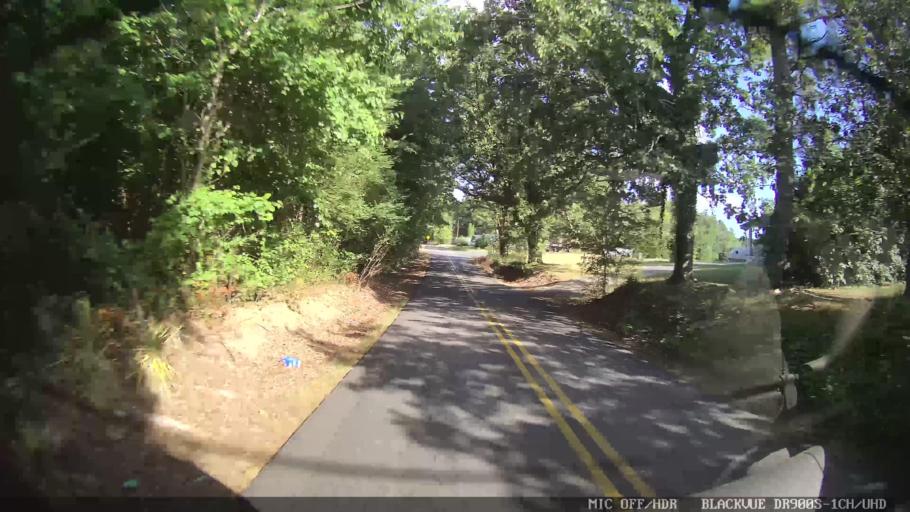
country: US
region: Georgia
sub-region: Floyd County
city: Rome
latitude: 34.2171
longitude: -85.1309
